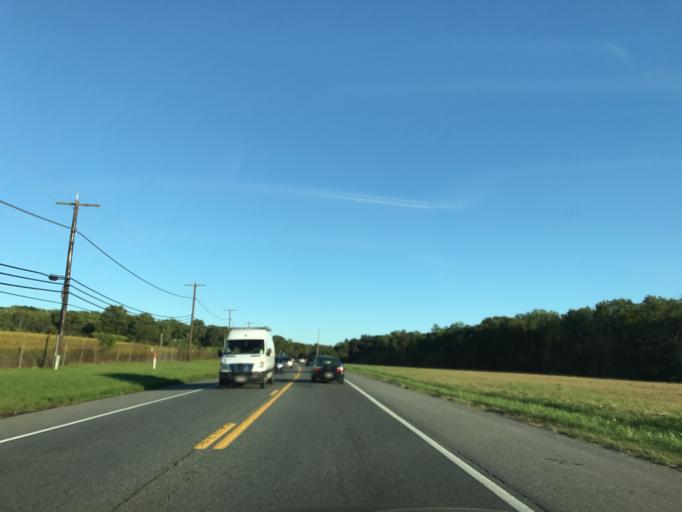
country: US
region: Maryland
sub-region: Prince George's County
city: Greenbelt
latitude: 39.0146
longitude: -76.8960
